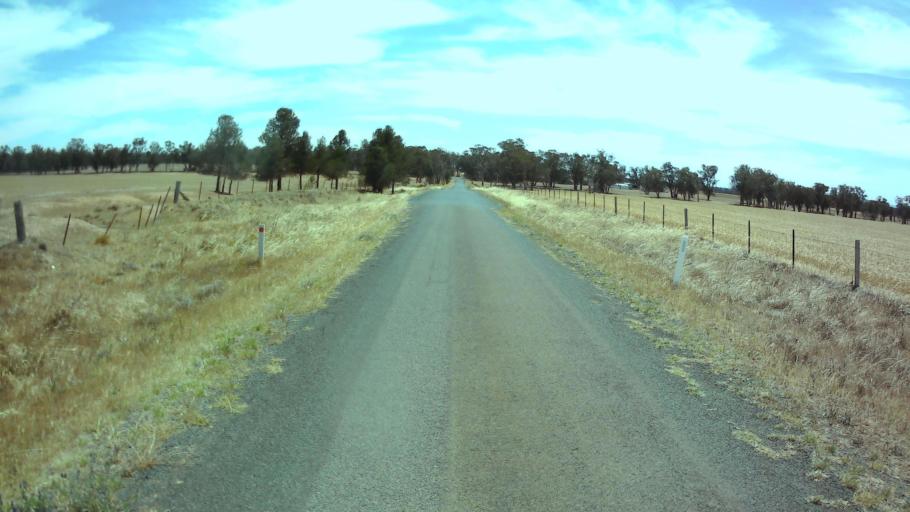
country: AU
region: New South Wales
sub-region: Weddin
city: Grenfell
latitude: -33.7439
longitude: 148.2081
